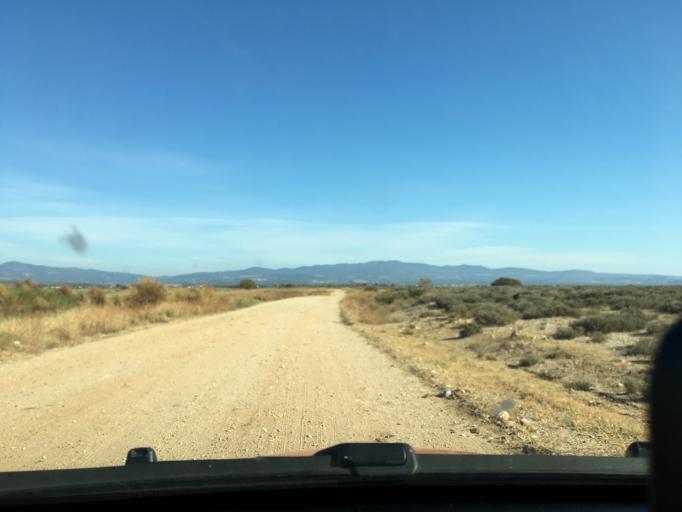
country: GR
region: Central Macedonia
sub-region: Nomos Chalkidikis
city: Nea Potidhaia
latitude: 40.2270
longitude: 23.3378
